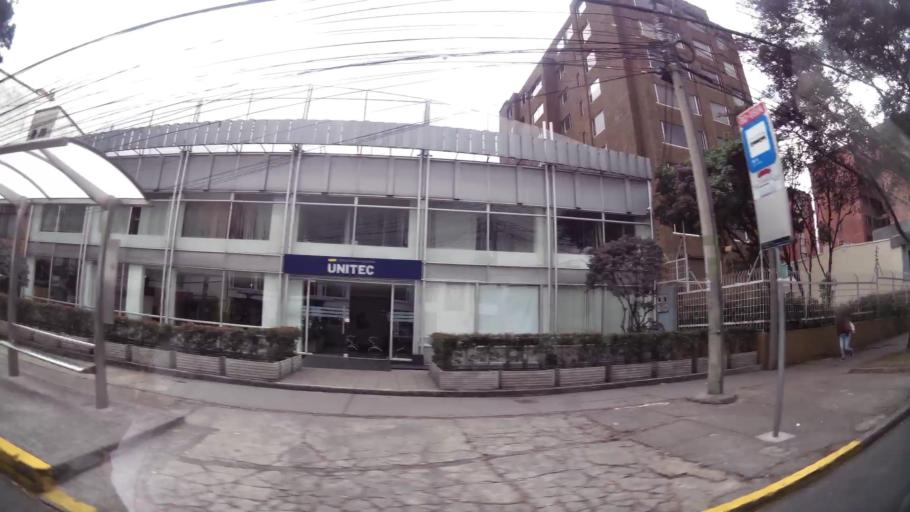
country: CO
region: Bogota D.C.
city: Barrio San Luis
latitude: 4.6618
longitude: -74.0575
